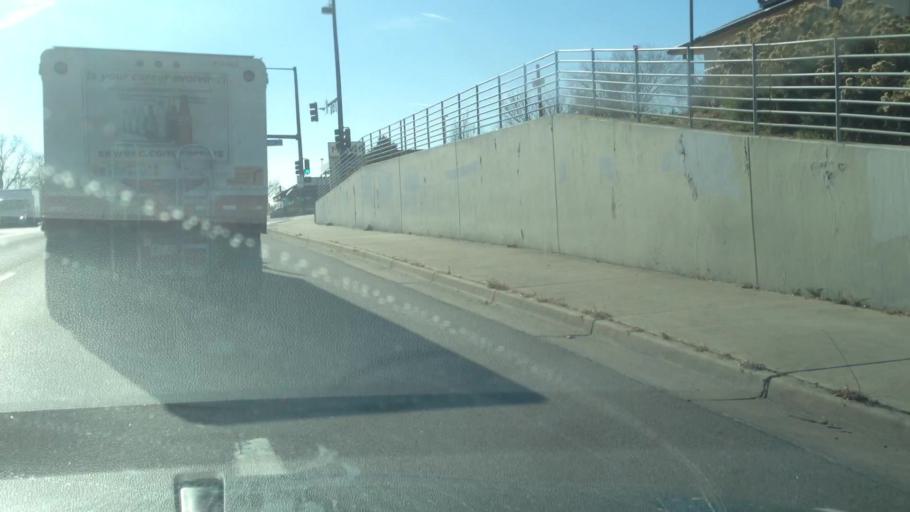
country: US
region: Colorado
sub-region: Jefferson County
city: Edgewater
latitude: 39.7246
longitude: -105.0534
